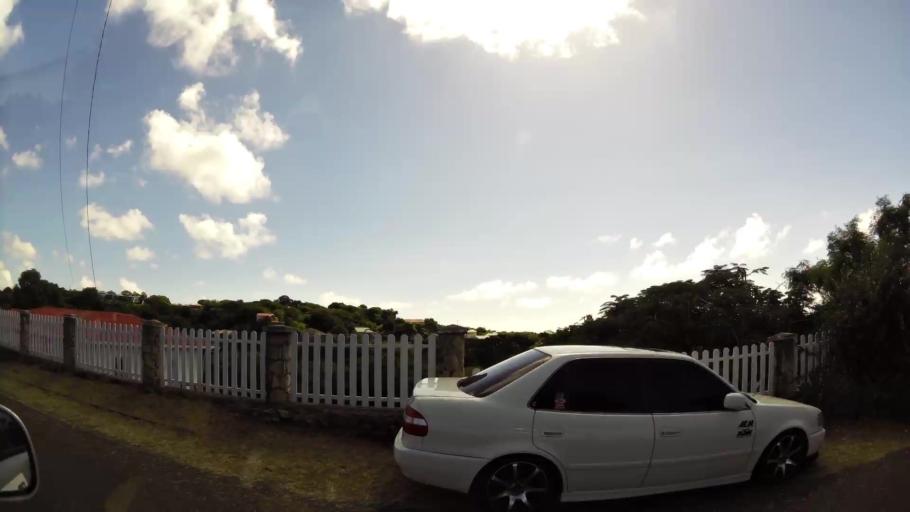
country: GD
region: Saint George
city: Saint George's
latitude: 11.9964
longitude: -61.7586
